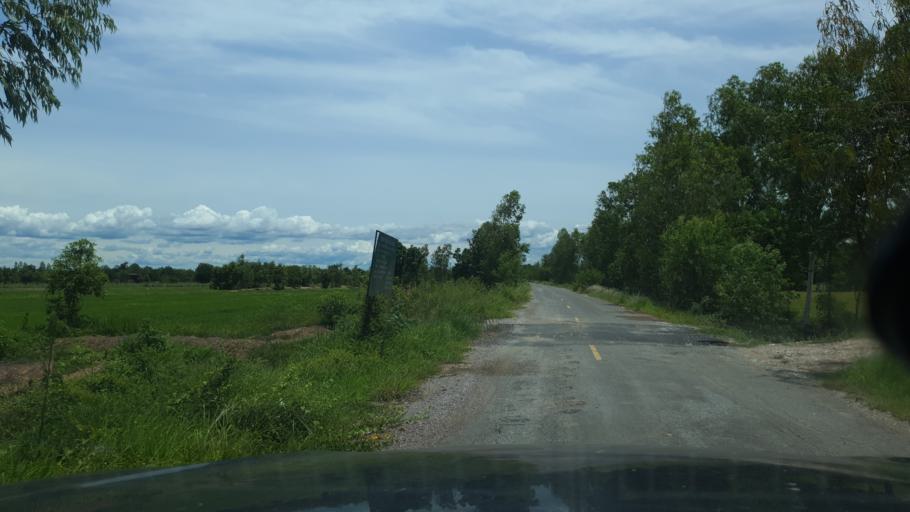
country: TH
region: Sukhothai
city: Ban Na
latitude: 17.1015
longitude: 99.6791
